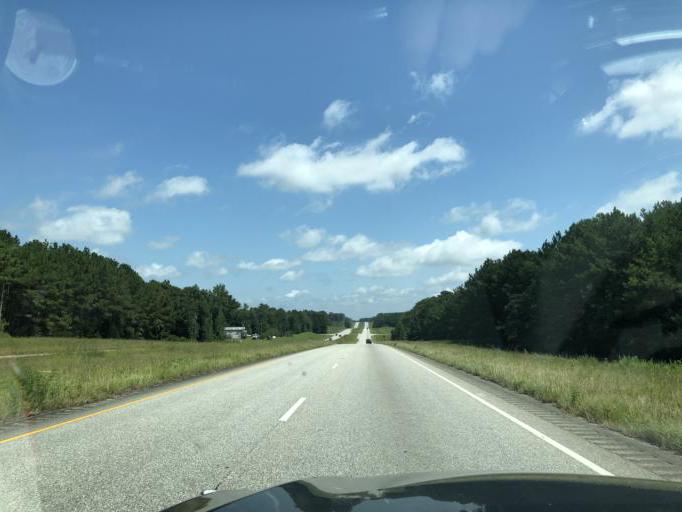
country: US
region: Alabama
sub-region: Barbour County
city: Eufaula
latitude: 31.7480
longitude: -85.2319
